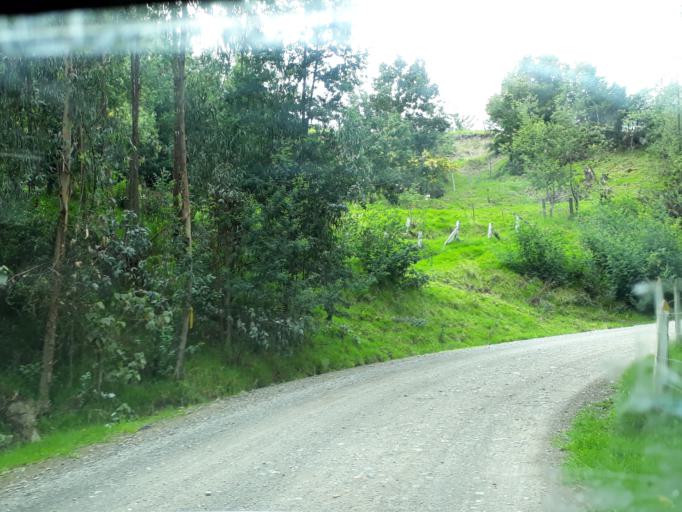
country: CO
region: Cundinamarca
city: La Mesa
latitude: 5.2961
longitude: -73.9048
